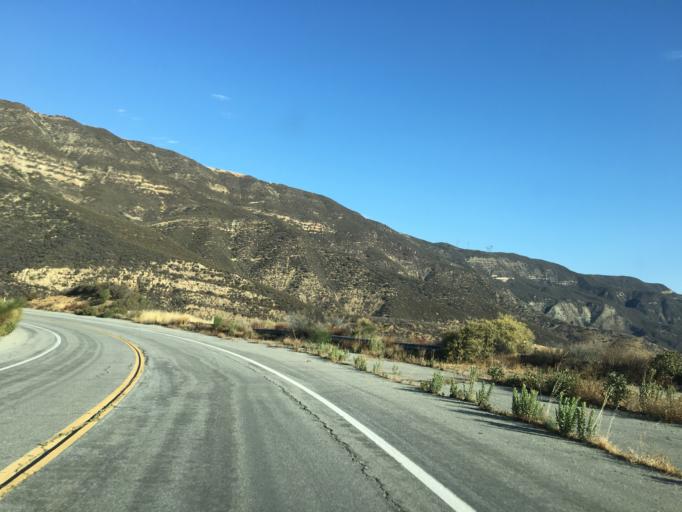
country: US
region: California
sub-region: Los Angeles County
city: Castaic
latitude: 34.5923
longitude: -118.6706
